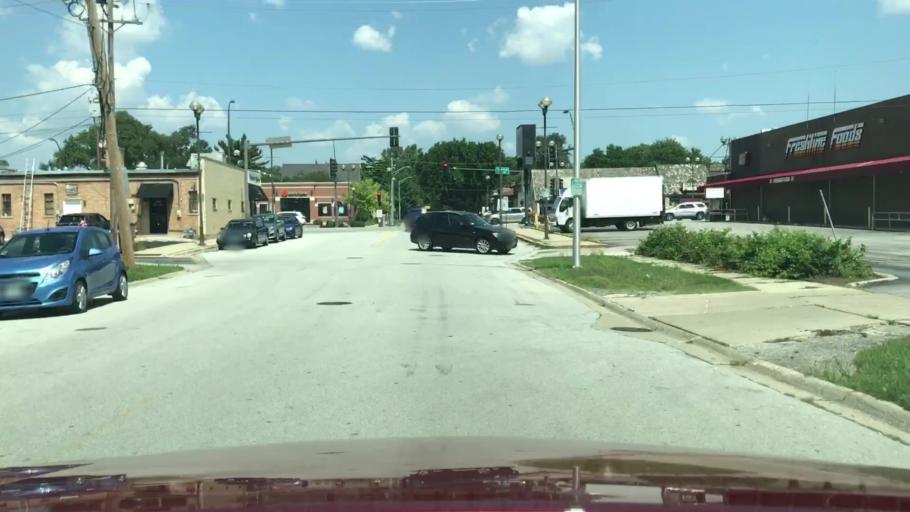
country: US
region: Illinois
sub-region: Cook County
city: Oak Lawn
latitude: 41.7190
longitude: -87.7555
